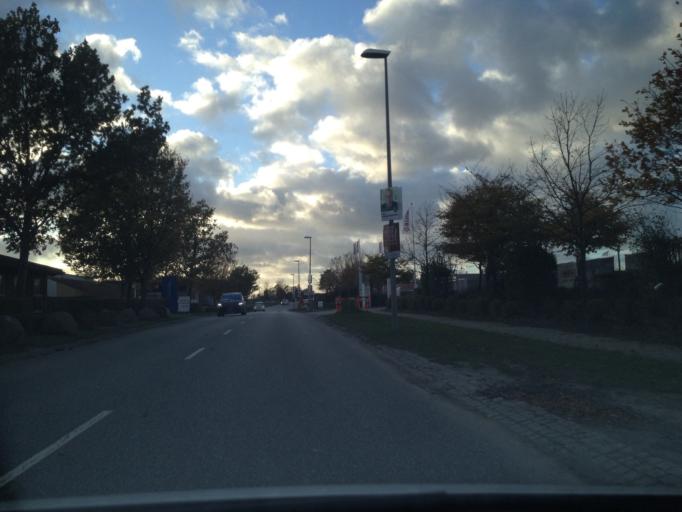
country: DK
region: Capital Region
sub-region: Hillerod Kommune
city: Hillerod
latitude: 55.9322
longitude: 12.2670
